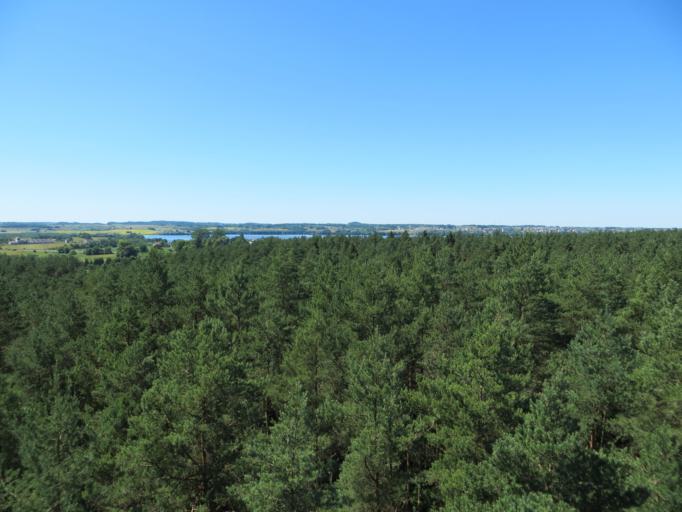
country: LT
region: Vilnius County
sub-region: Vilniaus Rajonas
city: Vievis
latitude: 54.7593
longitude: 24.8539
